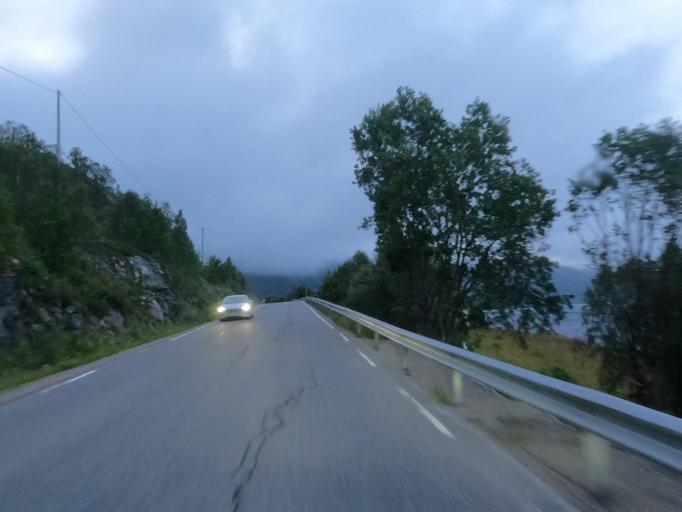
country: NO
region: Nordland
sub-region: Lodingen
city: Lodingen
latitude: 68.6087
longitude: 15.7775
